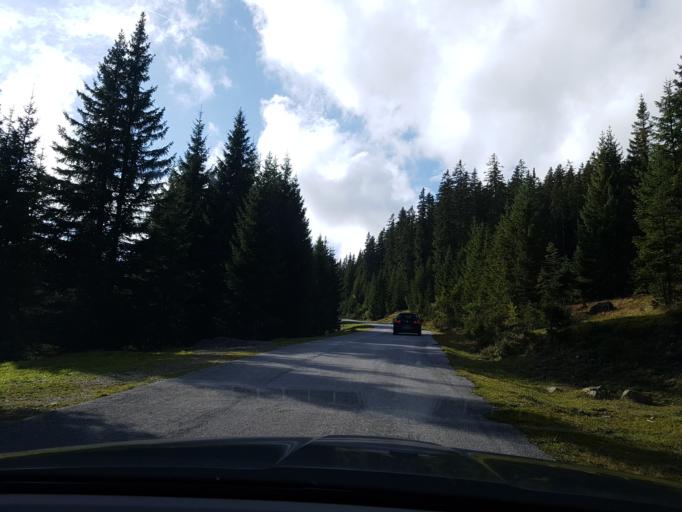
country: AT
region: Salzburg
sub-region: Politischer Bezirk Sankt Johann im Pongau
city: Radstadt
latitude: 47.4062
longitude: 13.4833
